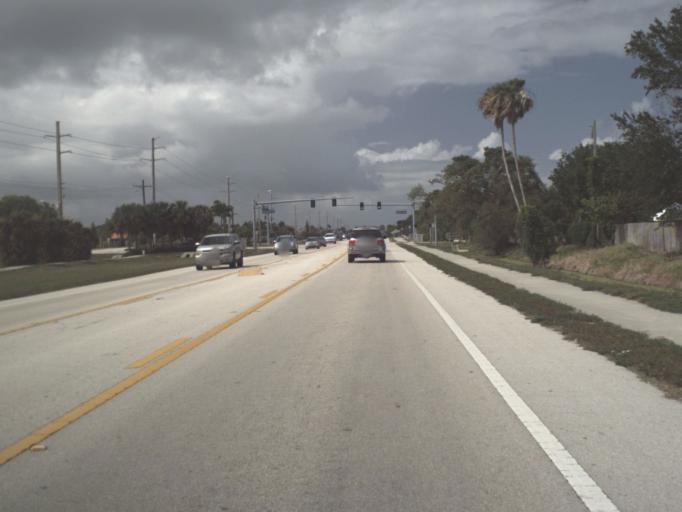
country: US
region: Florida
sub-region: Brevard County
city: South Patrick Shores
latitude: 28.1990
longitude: -80.6063
